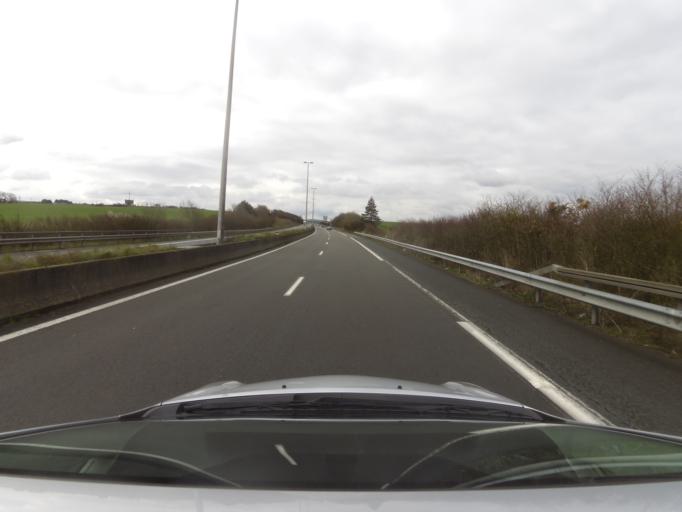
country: FR
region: Nord-Pas-de-Calais
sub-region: Departement du Pas-de-Calais
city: Marquise
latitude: 50.8327
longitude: 1.7032
